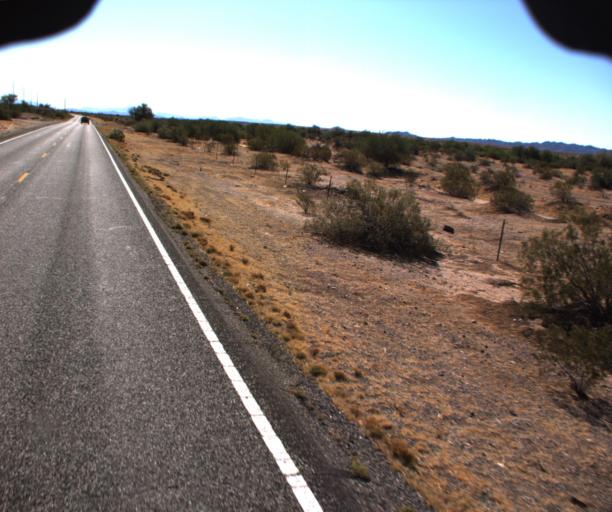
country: US
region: Arizona
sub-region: La Paz County
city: Parker
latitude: 33.9950
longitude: -114.1754
